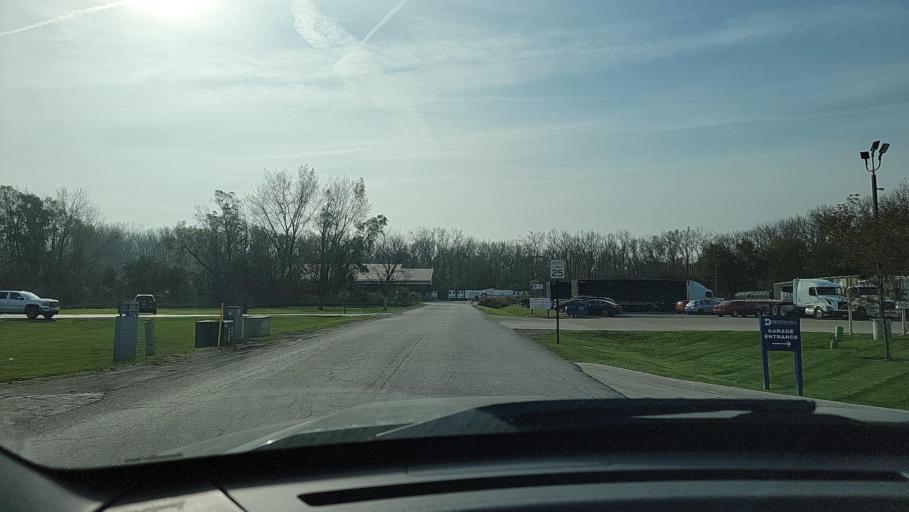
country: US
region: Indiana
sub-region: Porter County
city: Ogden Dunes
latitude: 41.6158
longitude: -87.1635
